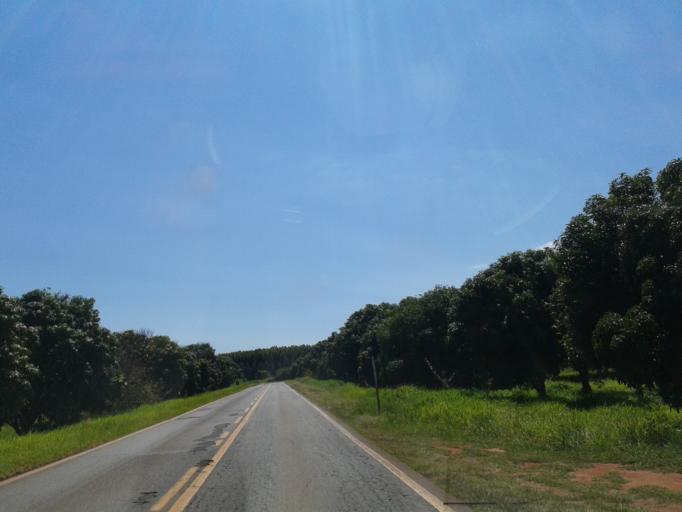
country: BR
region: Minas Gerais
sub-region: Centralina
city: Centralina
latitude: -18.7216
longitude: -49.1513
